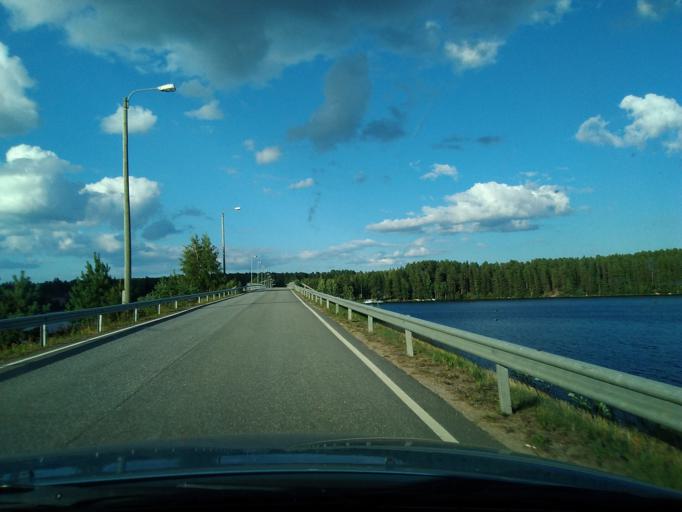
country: FI
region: Central Finland
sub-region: Saarijaervi-Viitasaari
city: Saarijaervi
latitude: 62.7056
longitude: 25.2041
